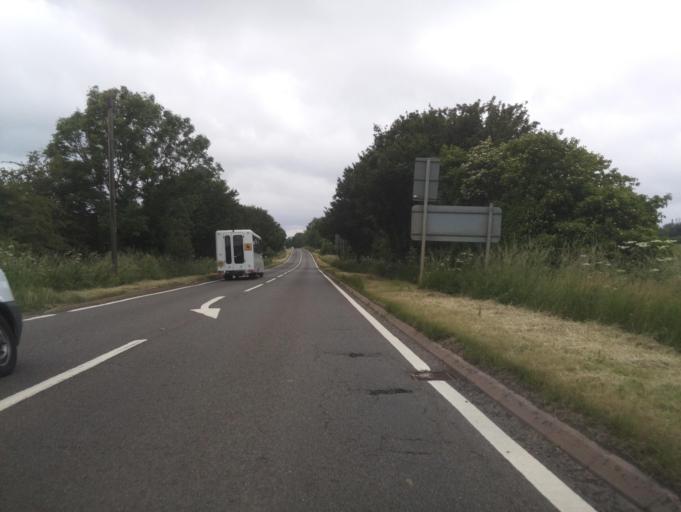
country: GB
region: England
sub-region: Leicestershire
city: Houghton on the Hill
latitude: 52.6209
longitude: -0.9612
